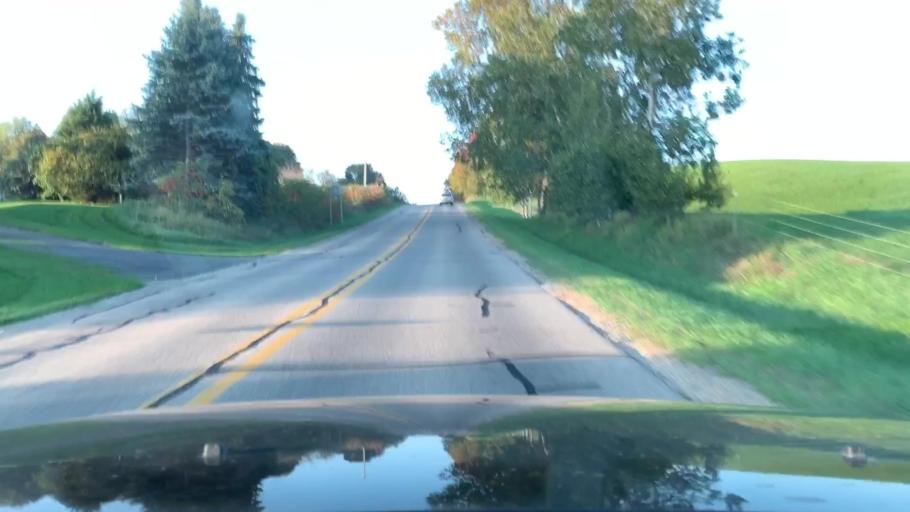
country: US
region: Michigan
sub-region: Kent County
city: Byron Center
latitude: 42.8135
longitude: -85.8026
